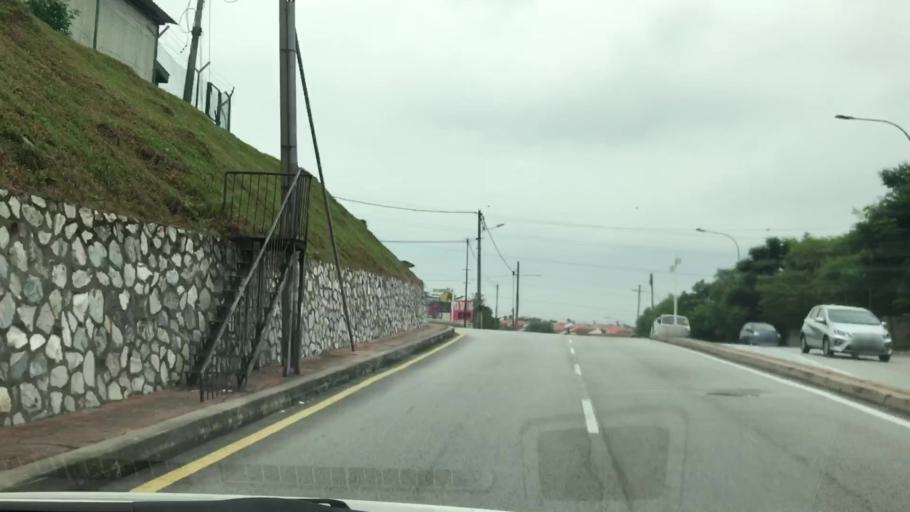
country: MY
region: Selangor
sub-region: Petaling
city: Petaling Jaya
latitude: 3.1110
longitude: 101.6185
